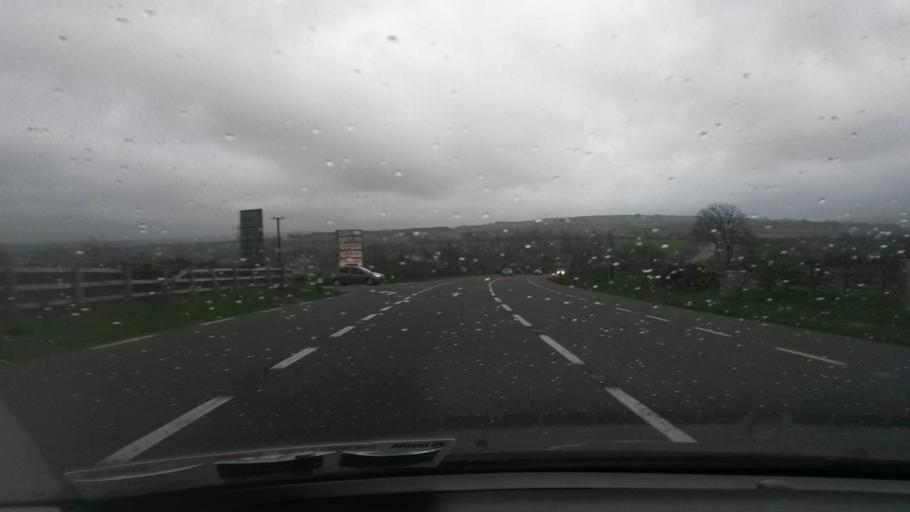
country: IE
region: Munster
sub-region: County Limerick
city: Abbeyfeale
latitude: 52.3588
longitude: -9.3248
